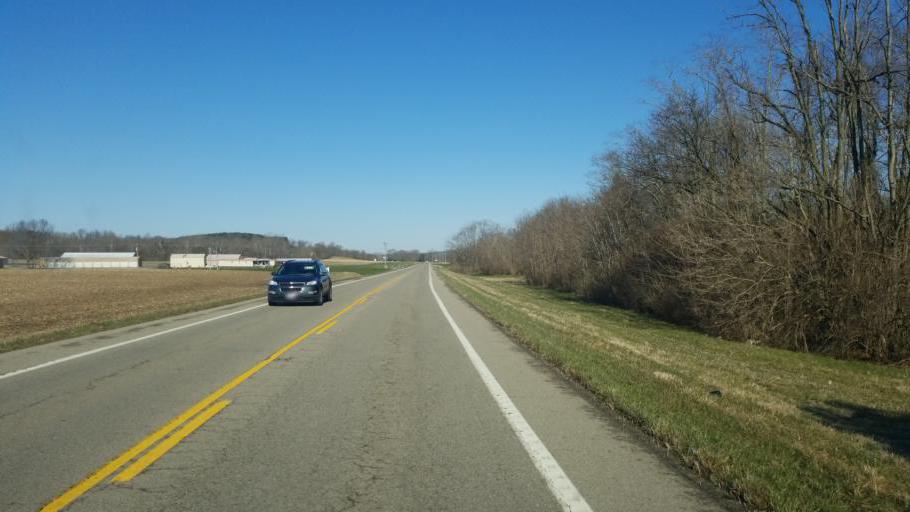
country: US
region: Ohio
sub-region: Highland County
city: Greenfield
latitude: 39.2237
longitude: -83.3117
